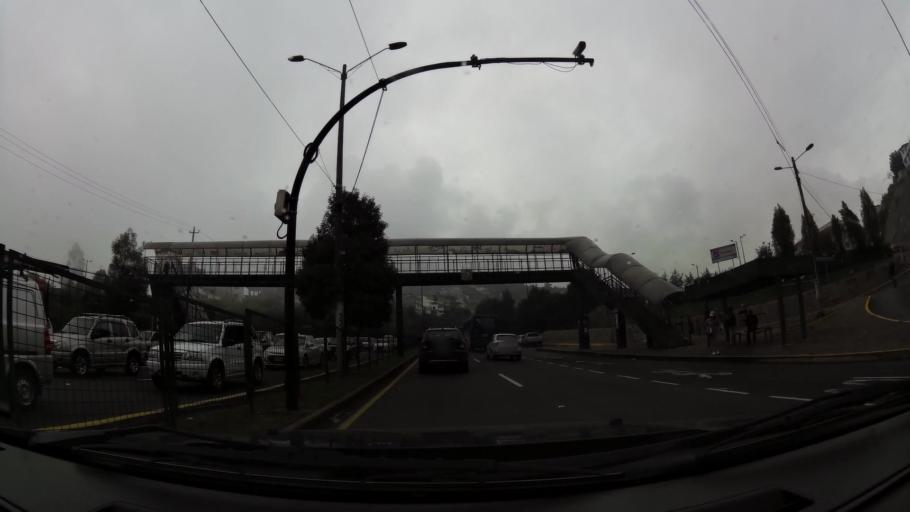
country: EC
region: Pichincha
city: Quito
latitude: -0.2278
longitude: -78.4867
